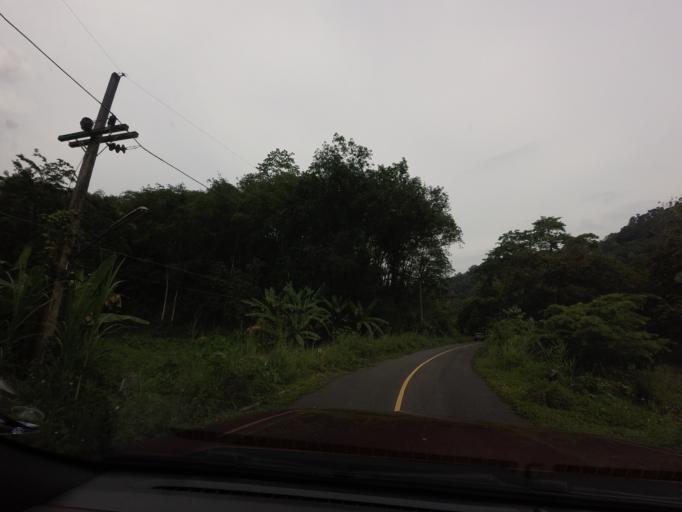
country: TH
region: Narathiwat
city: Si Sakhon
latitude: 6.0629
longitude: 101.3860
